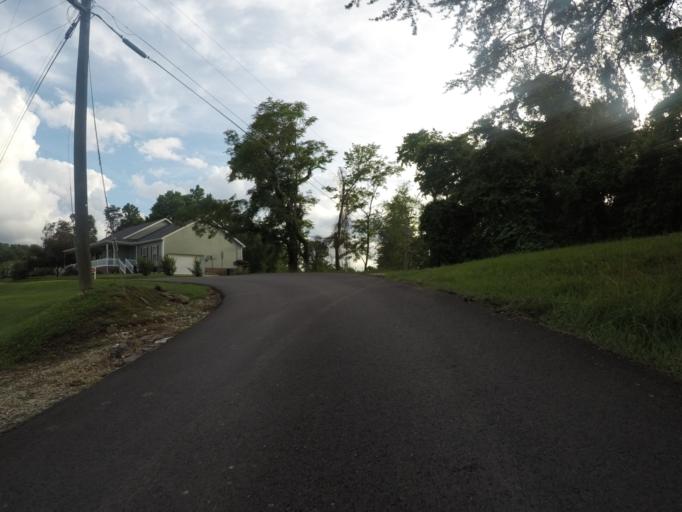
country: US
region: West Virginia
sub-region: Cabell County
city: Pea Ridge
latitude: 38.4057
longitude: -82.3584
